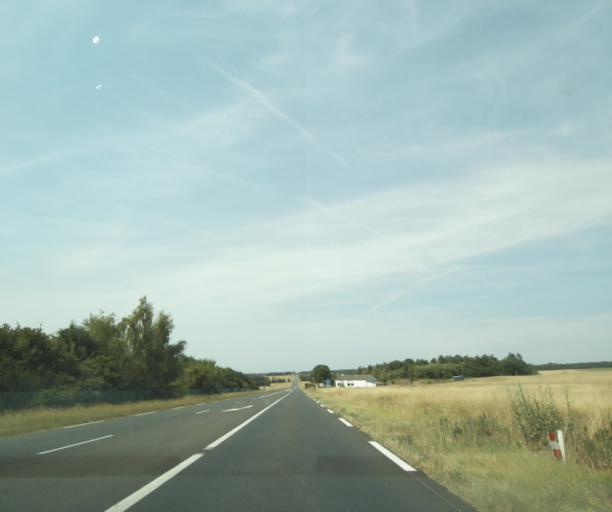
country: FR
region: Centre
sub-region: Departement d'Indre-et-Loire
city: Sainte-Maure-de-Touraine
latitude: 47.0727
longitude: 0.6138
